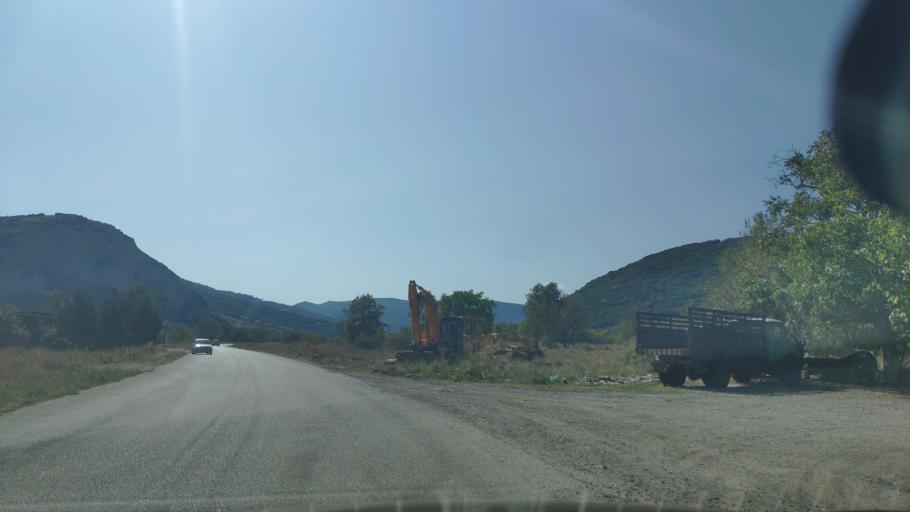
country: GR
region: Peloponnese
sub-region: Nomos Korinthias
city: Nemea
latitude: 37.9225
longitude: 22.5264
